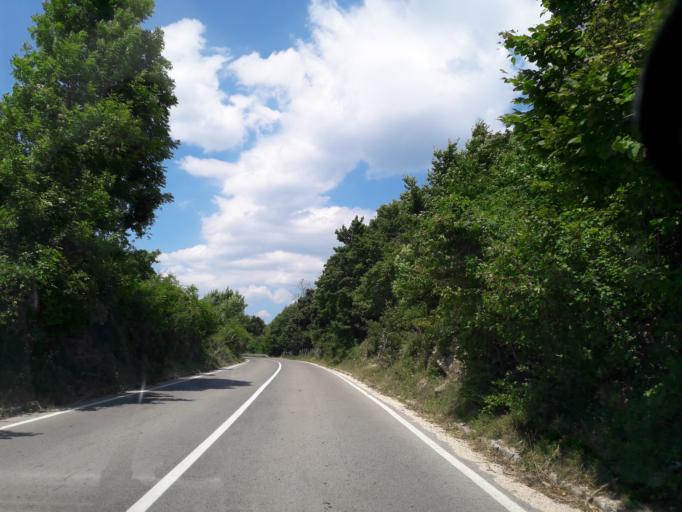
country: BA
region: Republika Srpska
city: Sipovo
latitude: 44.1708
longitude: 17.1676
